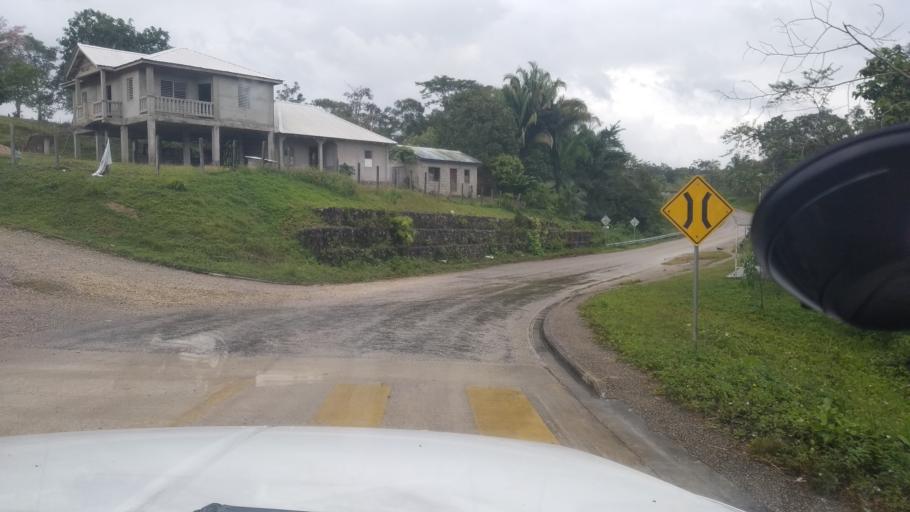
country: GT
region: Peten
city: San Luis
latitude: 16.2033
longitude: -89.1435
